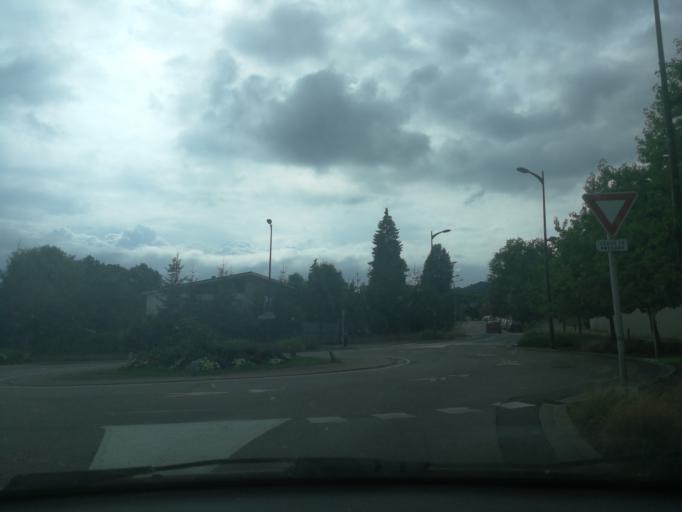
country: FR
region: Lorraine
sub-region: Departement de la Moselle
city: Thionville
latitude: 49.3716
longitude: 6.1504
